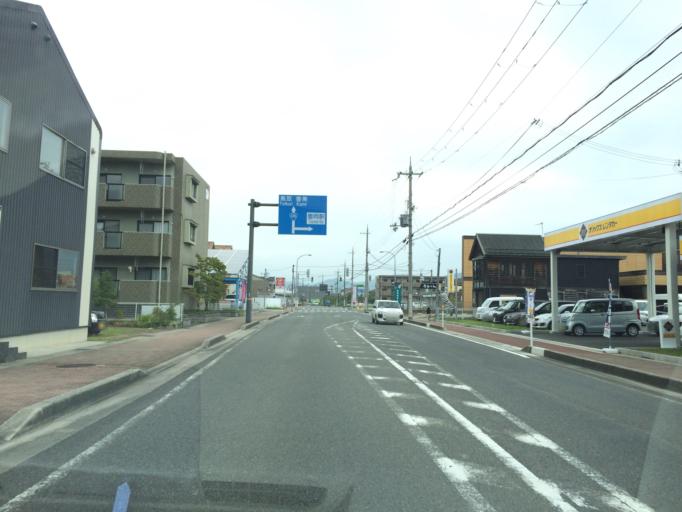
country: JP
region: Hyogo
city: Toyooka
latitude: 35.5425
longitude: 134.8099
